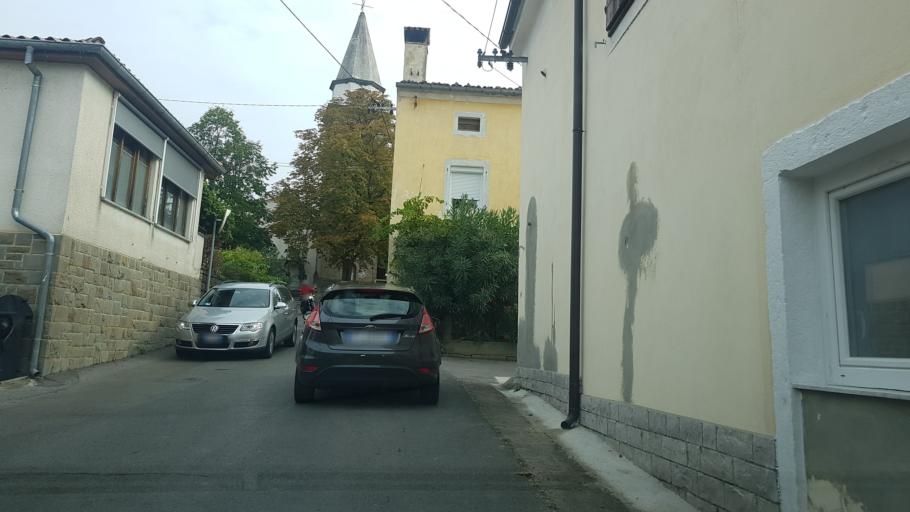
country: SI
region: Koper-Capodistria
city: Spodnje Skofije
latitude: 45.5733
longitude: 13.8022
